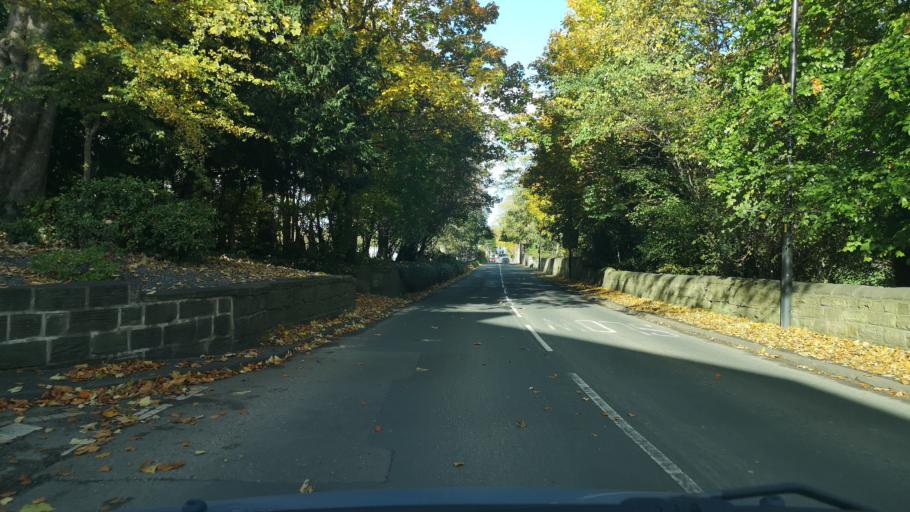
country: GB
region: England
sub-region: City and Borough of Wakefield
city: Low Ackworth
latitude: 53.6502
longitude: -1.3336
